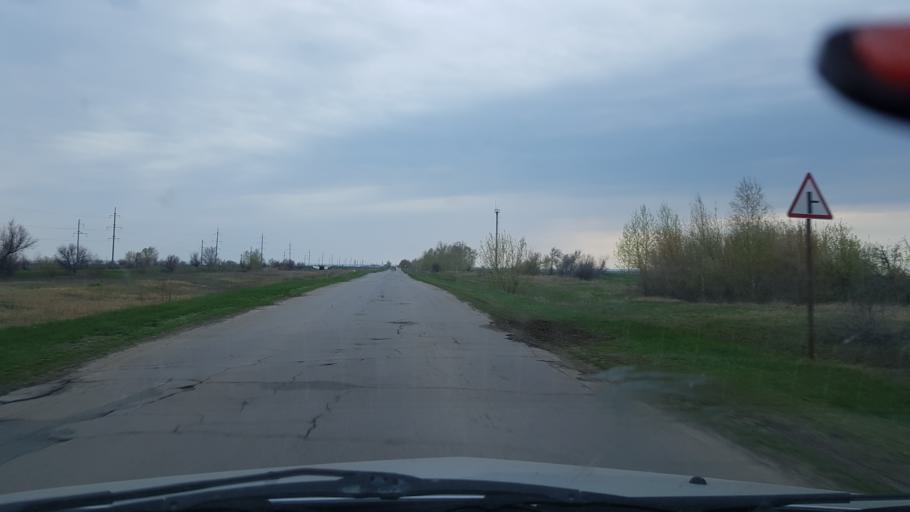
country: RU
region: Samara
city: Khryashchevka
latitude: 53.6688
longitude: 49.1328
